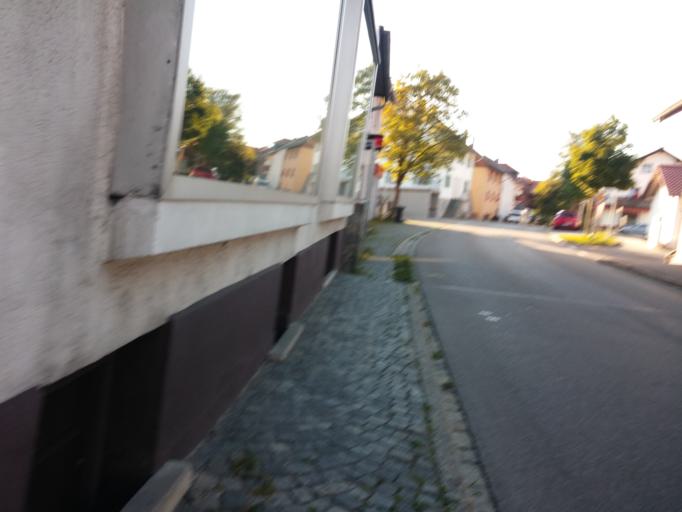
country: DE
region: Bavaria
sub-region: Swabia
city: Wiggensbach
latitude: 47.7460
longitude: 10.2300
